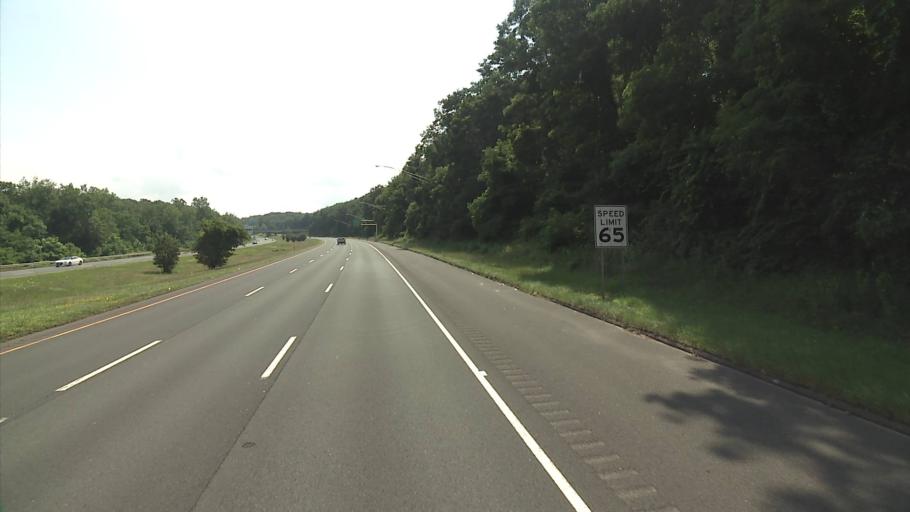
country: US
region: Connecticut
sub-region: Hartford County
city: Manchester
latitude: 41.7609
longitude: -72.5105
